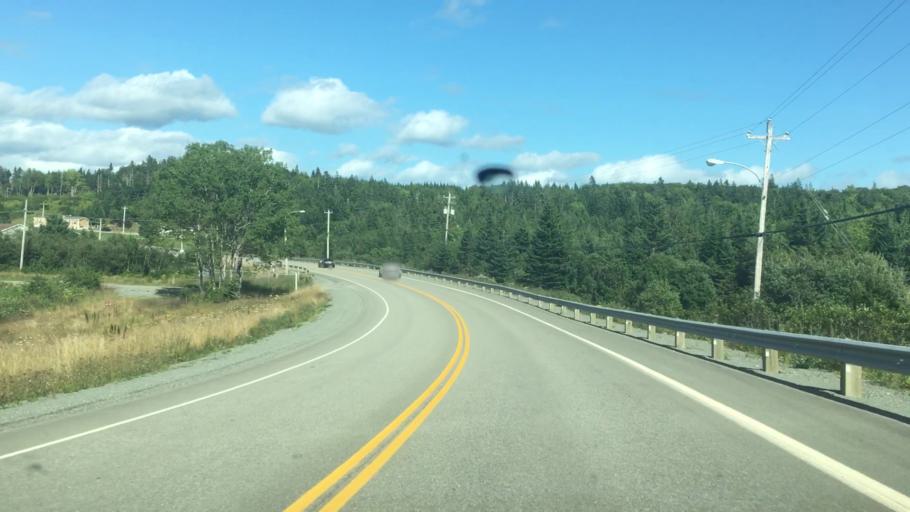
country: CA
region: Nova Scotia
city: Princeville
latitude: 45.6848
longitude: -60.7567
